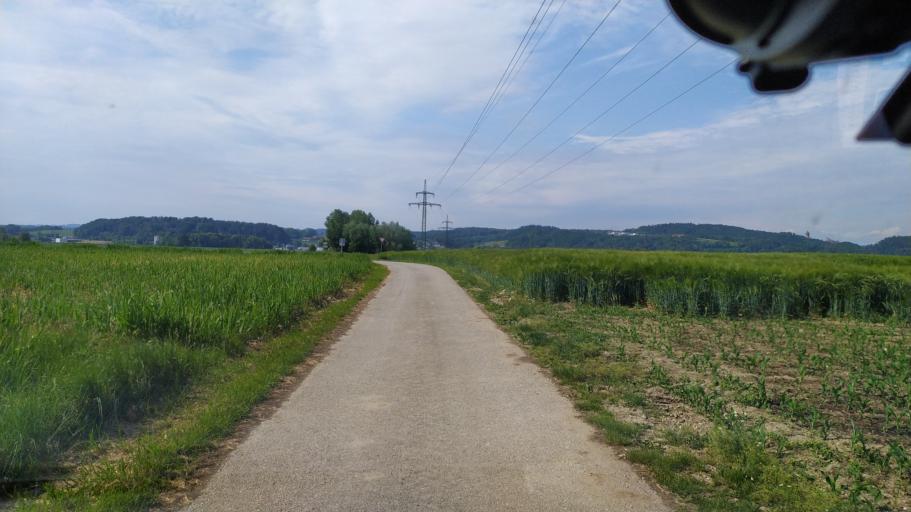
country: AT
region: Upper Austria
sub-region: Politischer Bezirk Perg
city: Bad Kreuzen
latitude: 48.1949
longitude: 14.7593
